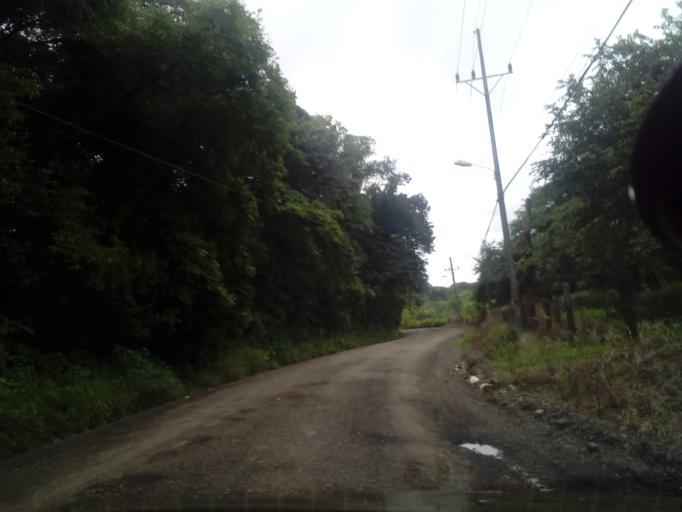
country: CR
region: Guanacaste
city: Samara
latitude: 9.9355
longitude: -85.6488
